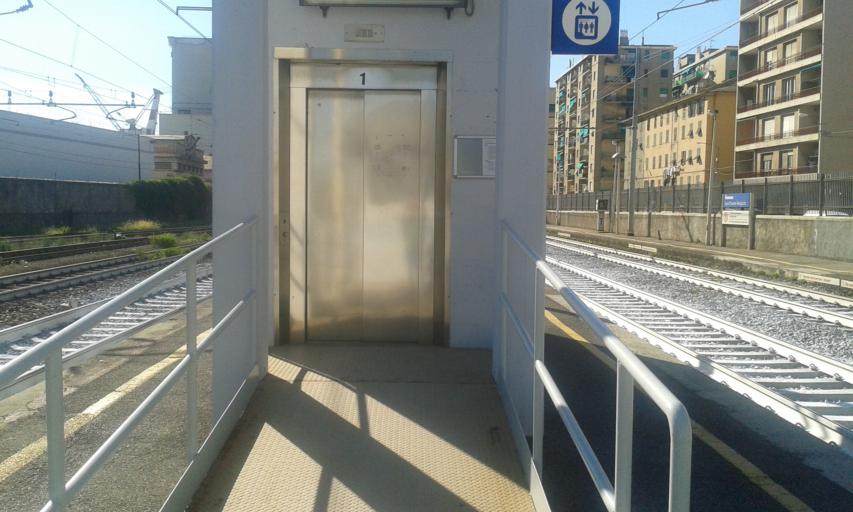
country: IT
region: Liguria
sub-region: Provincia di Genova
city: San Teodoro
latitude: 44.4224
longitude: 8.8469
